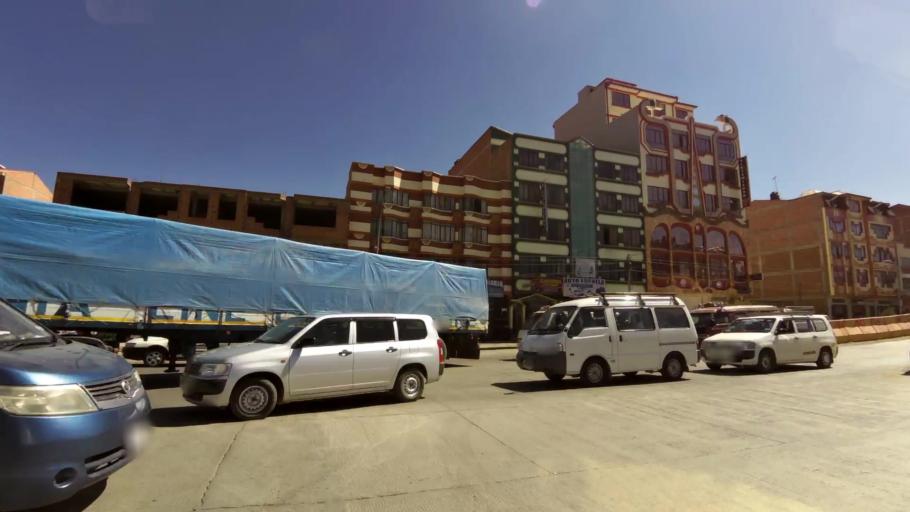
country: BO
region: La Paz
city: La Paz
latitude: -16.5358
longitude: -68.1917
